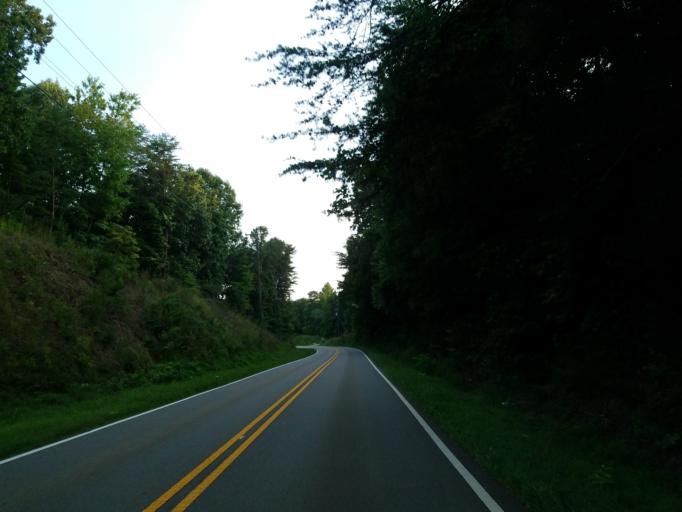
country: US
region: Georgia
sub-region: Pickens County
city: Jasper
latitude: 34.5451
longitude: -84.4723
